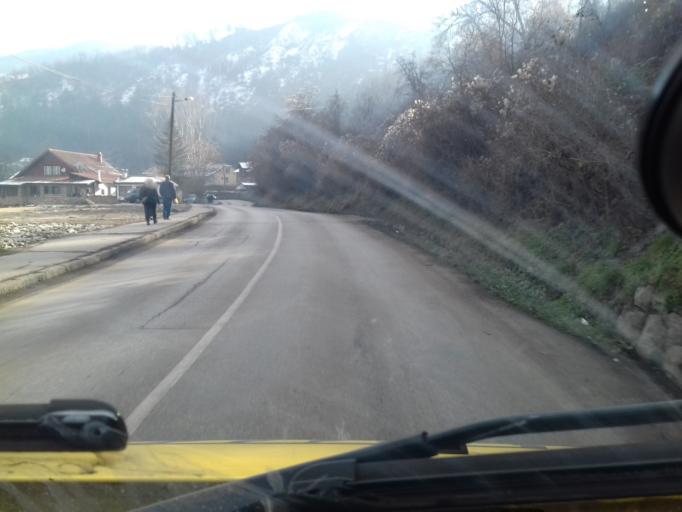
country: BA
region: Federation of Bosnia and Herzegovina
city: Zenica
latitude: 44.1891
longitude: 17.9191
